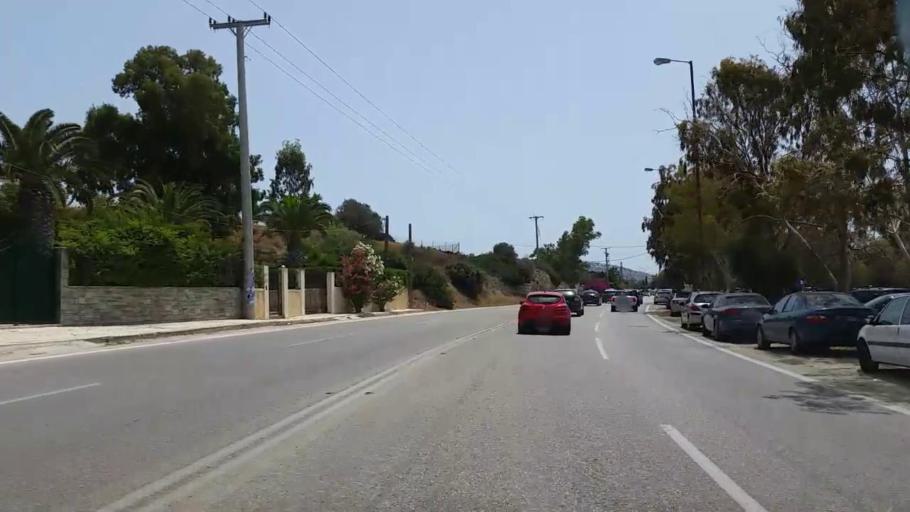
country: GR
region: Attica
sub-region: Nomarchia Anatolikis Attikis
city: Saronida
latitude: 37.7353
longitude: 23.9061
